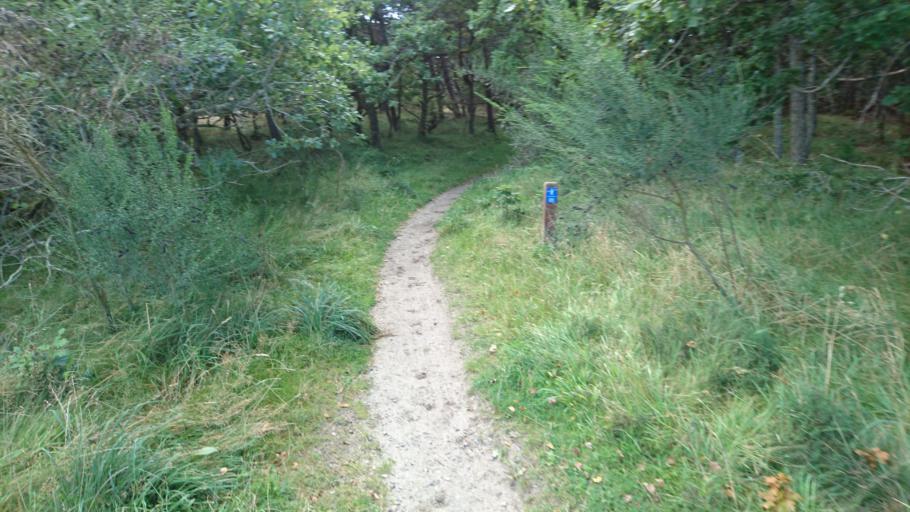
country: DK
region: North Denmark
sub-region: Frederikshavn Kommune
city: Skagen
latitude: 57.7209
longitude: 10.5291
